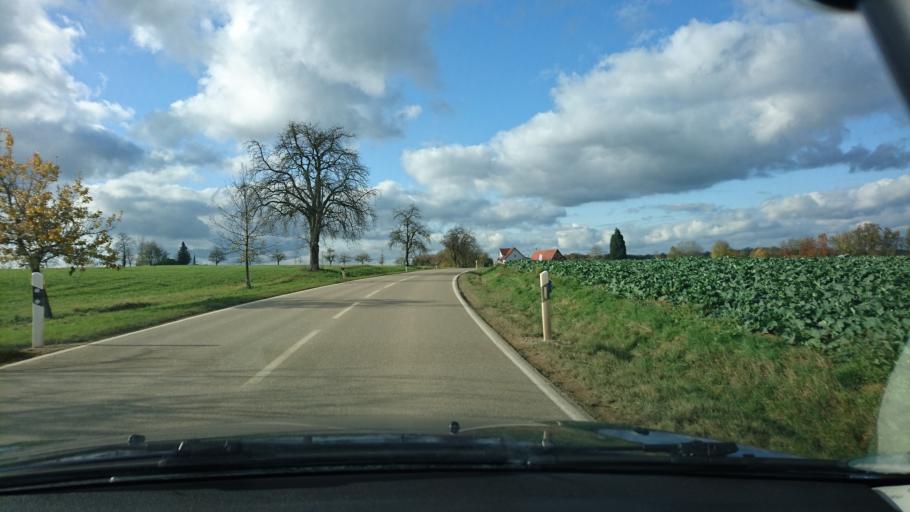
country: DE
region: Baden-Wuerttemberg
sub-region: Regierungsbezirk Stuttgart
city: Abtsgmund
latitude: 48.8915
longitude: 9.9724
